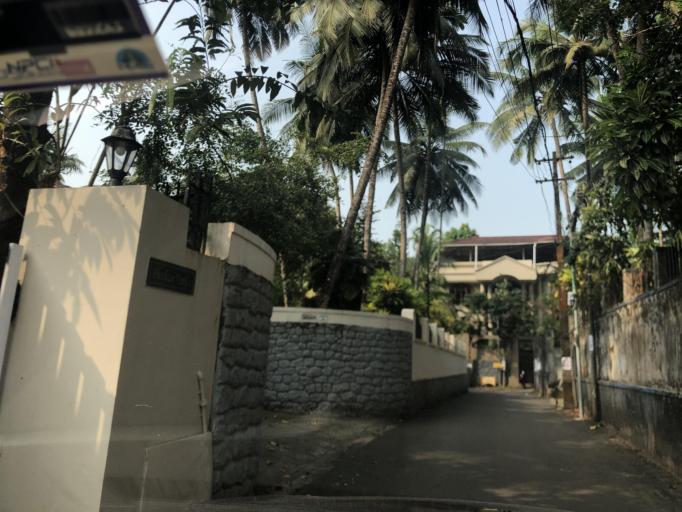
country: IN
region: Kerala
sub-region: Kozhikode
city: Kozhikode
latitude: 11.2783
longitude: 75.7784
